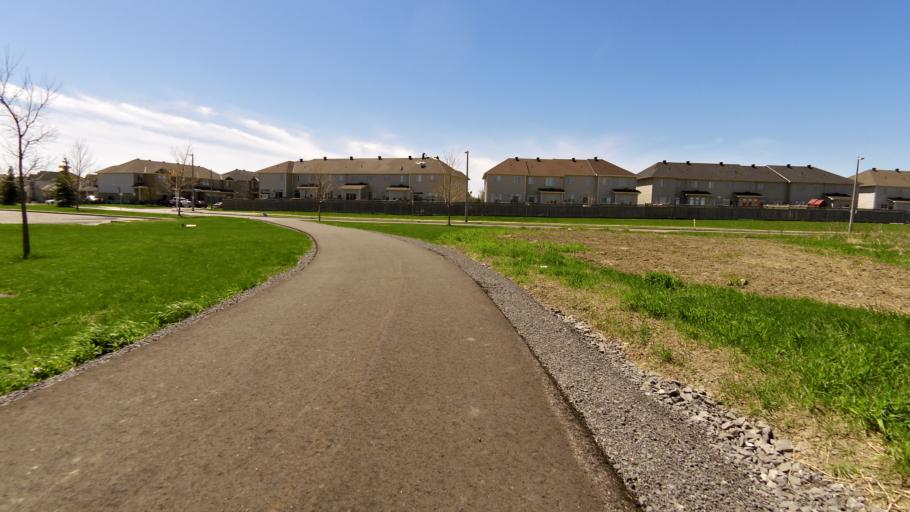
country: CA
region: Ontario
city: Clarence-Rockland
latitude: 45.4617
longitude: -75.4573
